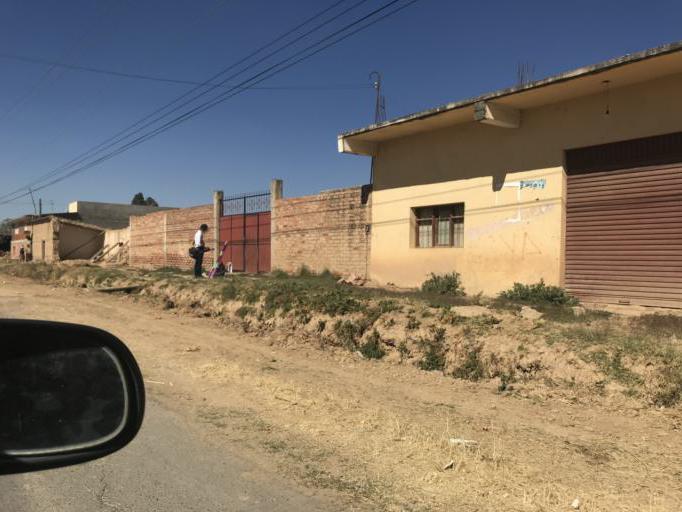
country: BO
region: Cochabamba
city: Cliza
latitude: -17.5963
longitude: -65.9513
